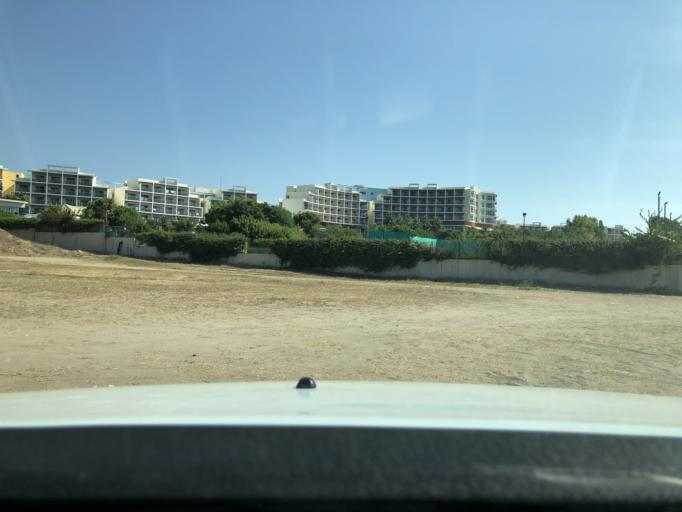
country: TR
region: Antalya
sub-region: Manavgat
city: Manavgat
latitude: 36.7567
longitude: 31.4248
